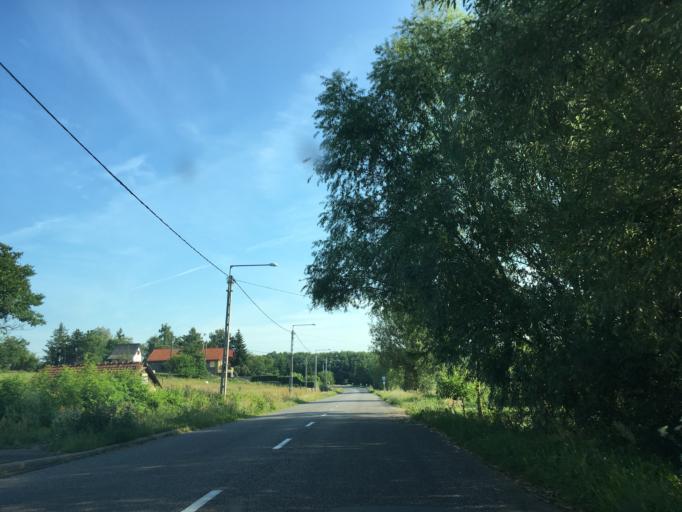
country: HU
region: Hajdu-Bihar
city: Hajdusamson
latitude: 47.5728
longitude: 21.7704
